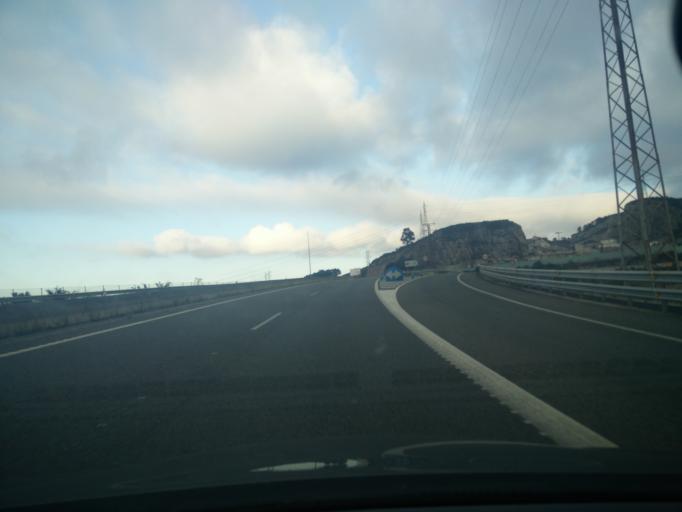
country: ES
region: Galicia
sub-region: Provincia da Coruna
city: A Coruna
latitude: 43.3424
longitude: -8.4462
